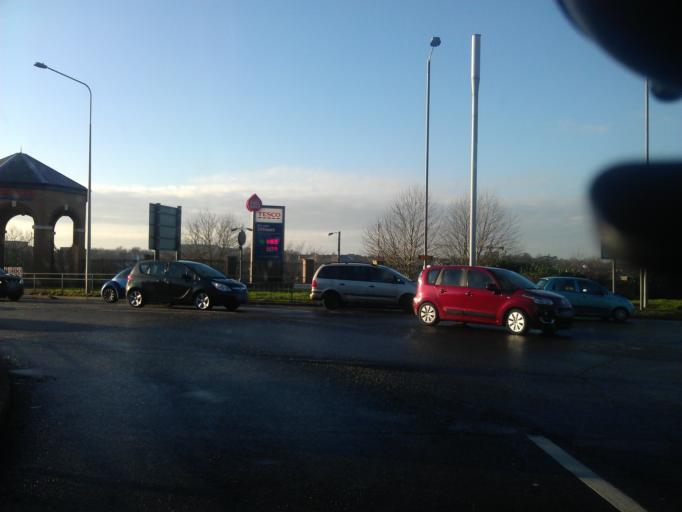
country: GB
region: England
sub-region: Essex
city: Colchester
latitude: 51.8841
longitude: 0.9327
